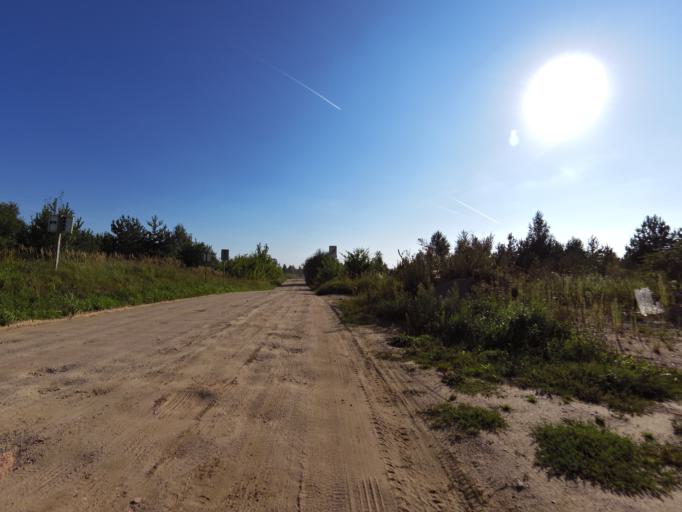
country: LT
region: Vilnius County
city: Pilaite
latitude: 54.7165
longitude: 25.1786
